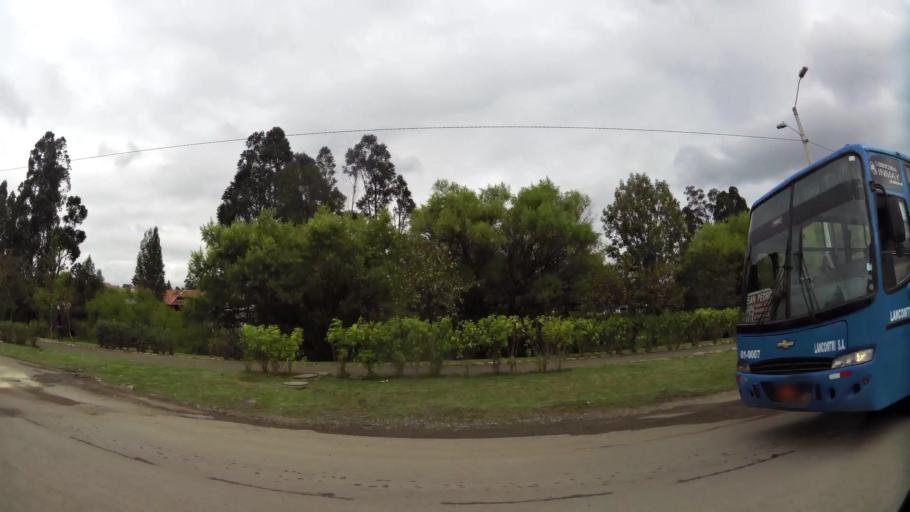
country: EC
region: Azuay
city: Cuenca
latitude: -2.8963
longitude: -78.9691
